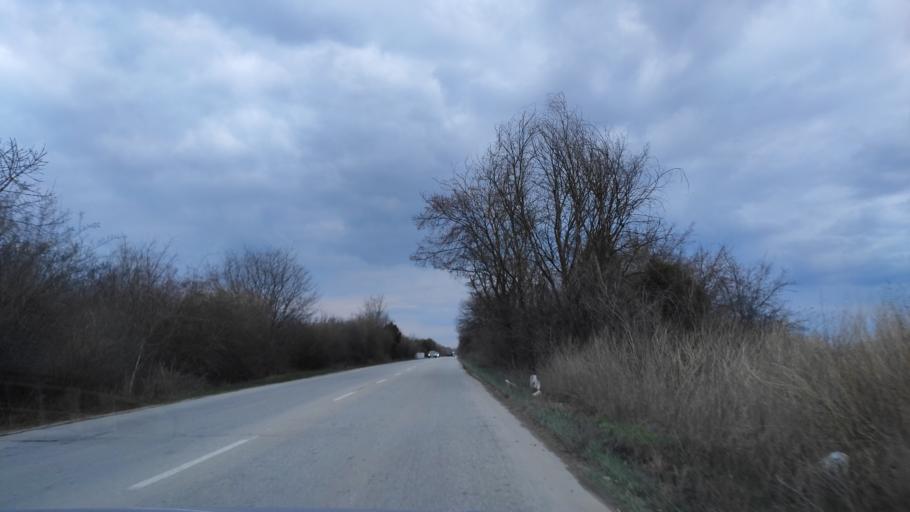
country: BG
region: Varna
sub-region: Obshtina Aksakovo
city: Aksakovo
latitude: 43.2291
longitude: 27.8305
